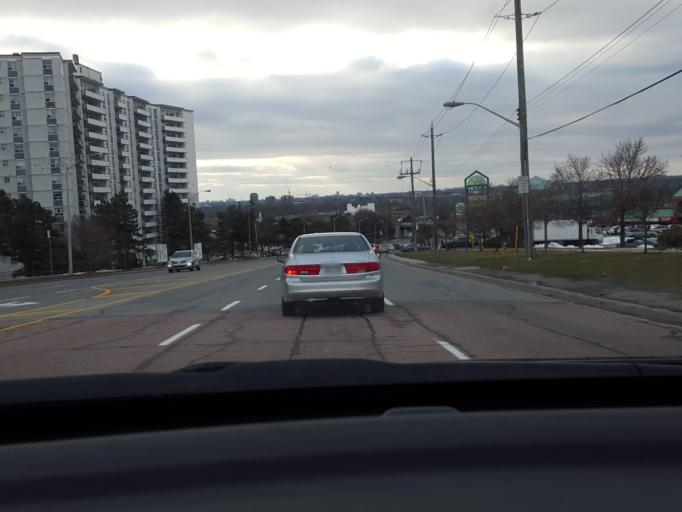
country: CA
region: Ontario
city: Scarborough
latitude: 43.7420
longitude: -79.3107
